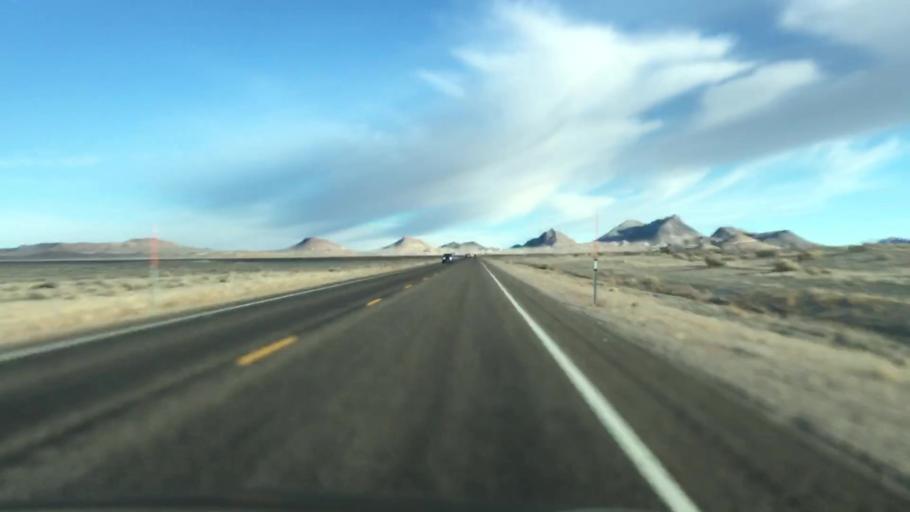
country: US
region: Nevada
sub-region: Nye County
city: Tonopah
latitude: 38.0970
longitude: -117.3188
